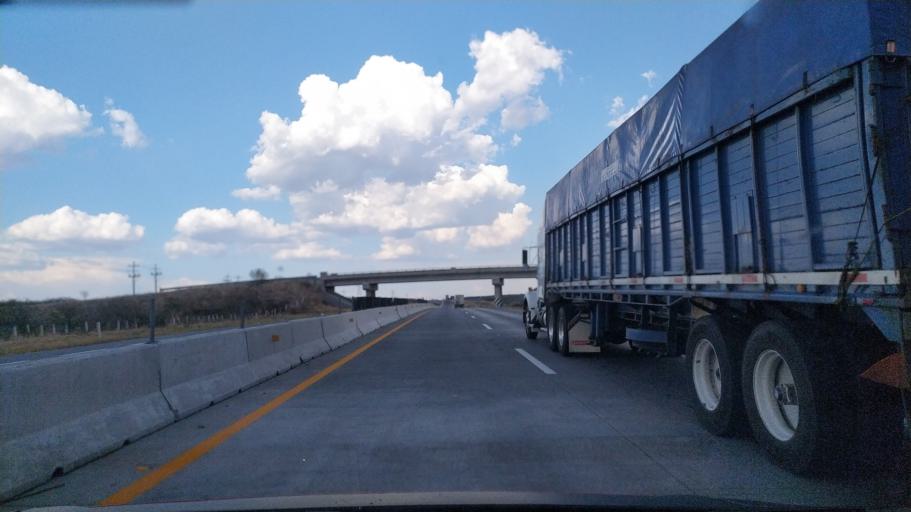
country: MX
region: Michoacan
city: La Piedad Cavadas
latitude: 20.3949
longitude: -102.0775
